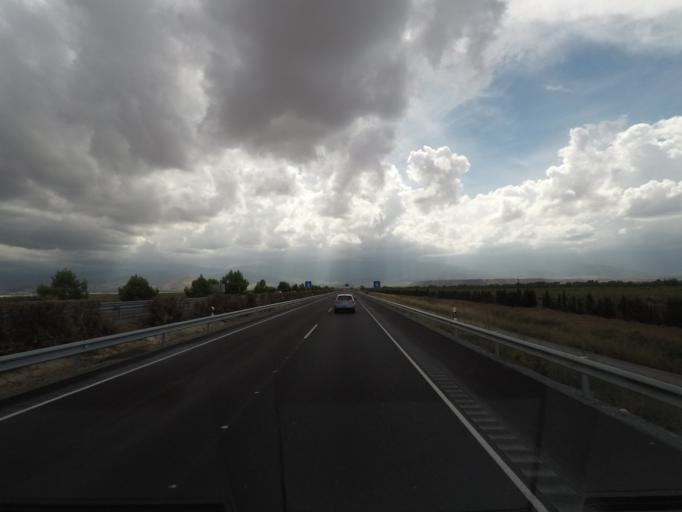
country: ES
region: Andalusia
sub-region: Provincia de Granada
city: Albunan
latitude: 37.2396
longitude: -3.0821
